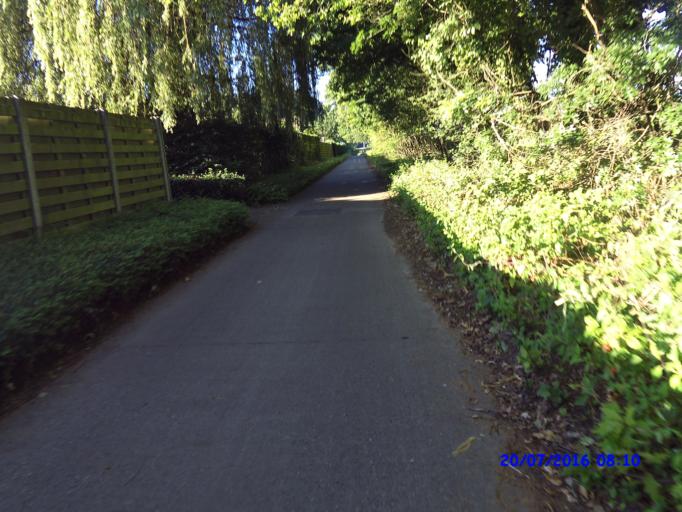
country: BE
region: Flanders
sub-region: Provincie Antwerpen
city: Turnhout
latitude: 51.3062
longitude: 4.9297
